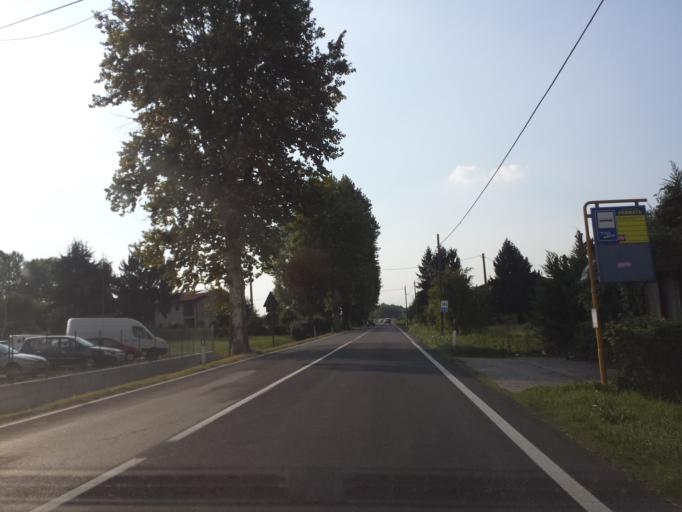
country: IT
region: Veneto
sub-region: Provincia di Vicenza
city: Grumolo delle Abbadesse
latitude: 45.4883
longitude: 11.6731
